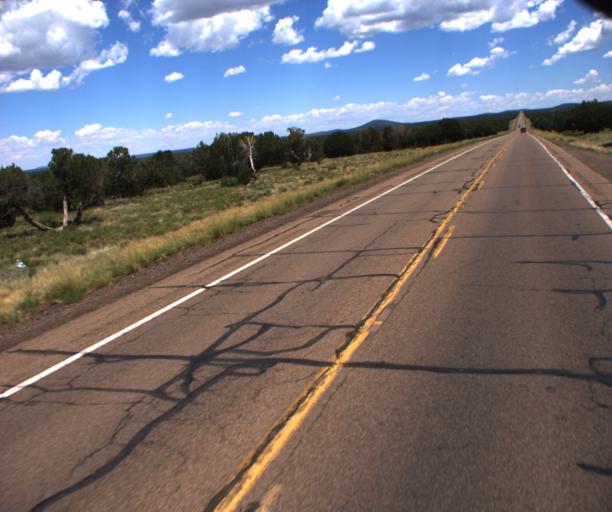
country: US
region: Arizona
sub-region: Navajo County
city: Show Low
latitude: 34.2644
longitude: -109.9602
